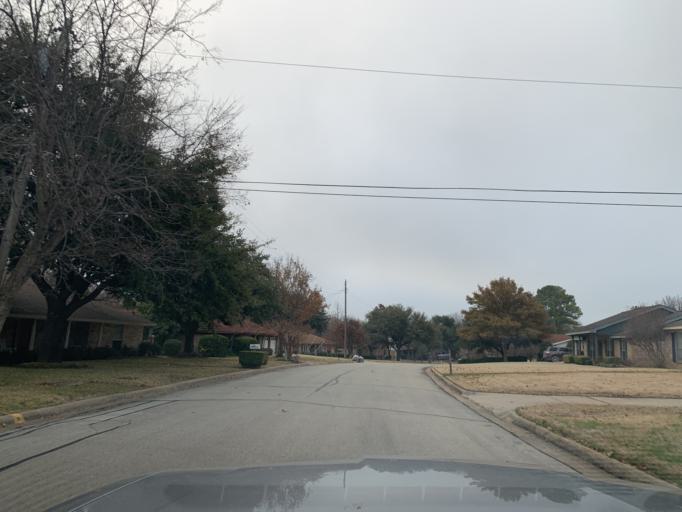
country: US
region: Texas
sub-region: Tarrant County
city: Bedford
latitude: 32.8370
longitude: -97.1528
